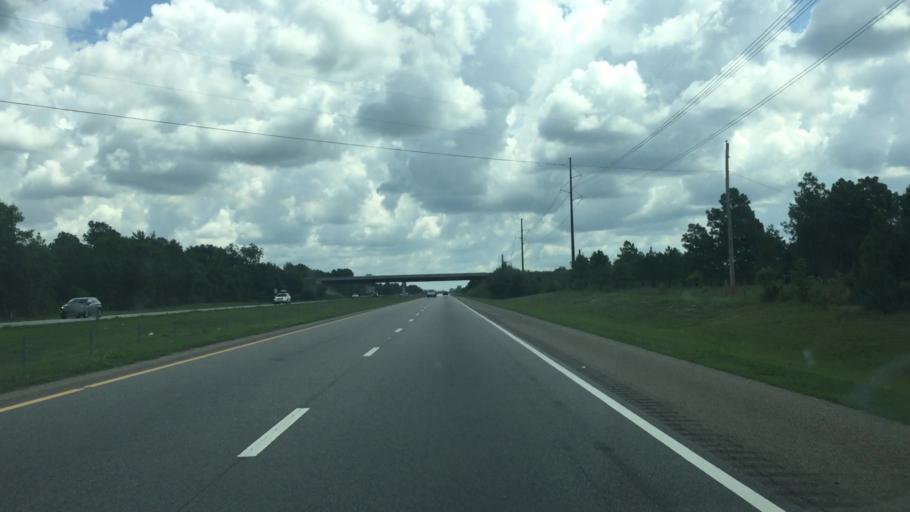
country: US
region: North Carolina
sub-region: Richmond County
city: Hamlet
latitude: 34.8596
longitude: -79.6793
